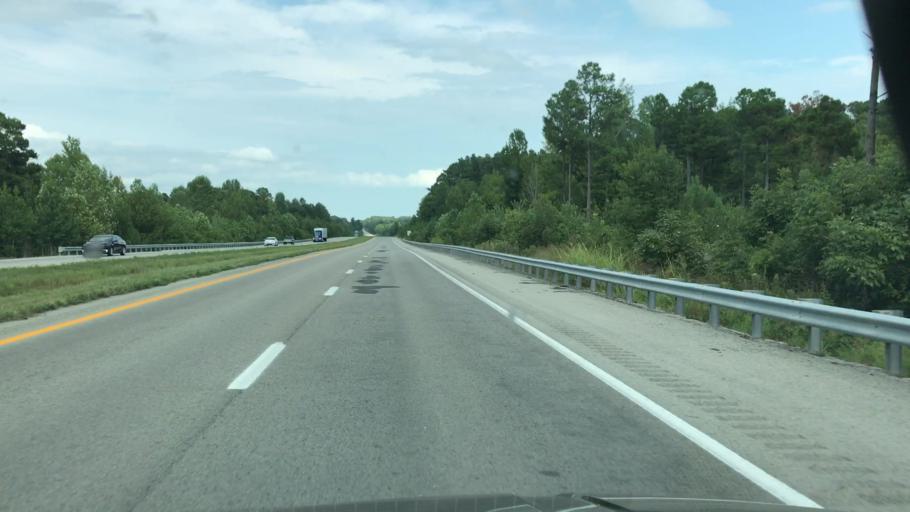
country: US
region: Kentucky
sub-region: Hopkins County
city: Earlington
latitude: 37.2015
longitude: -87.5314
